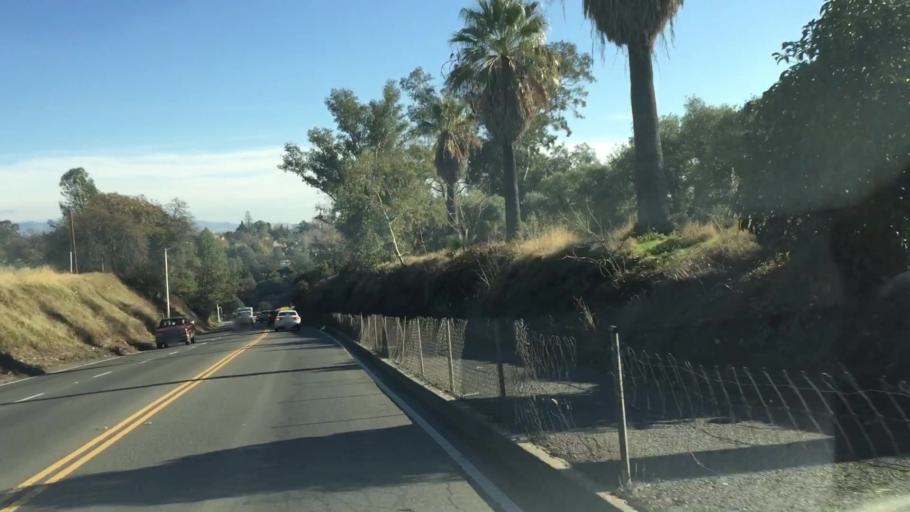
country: US
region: California
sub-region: Butte County
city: Oroville
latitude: 39.5204
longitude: -121.5533
